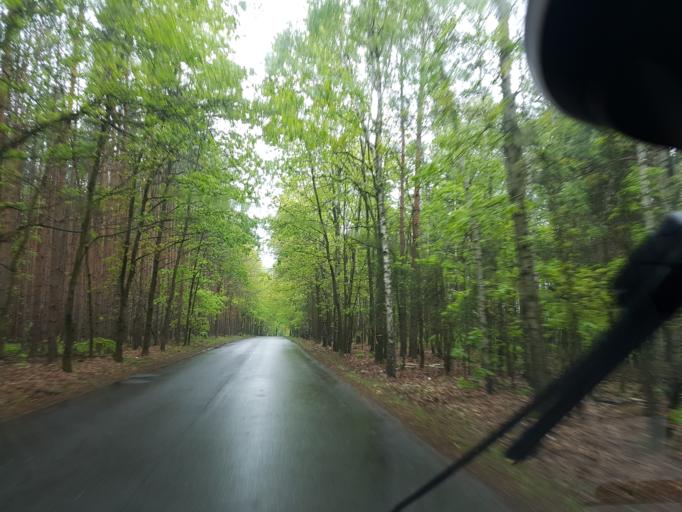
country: DE
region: Brandenburg
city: Tschernitz
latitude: 51.6302
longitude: 14.6043
